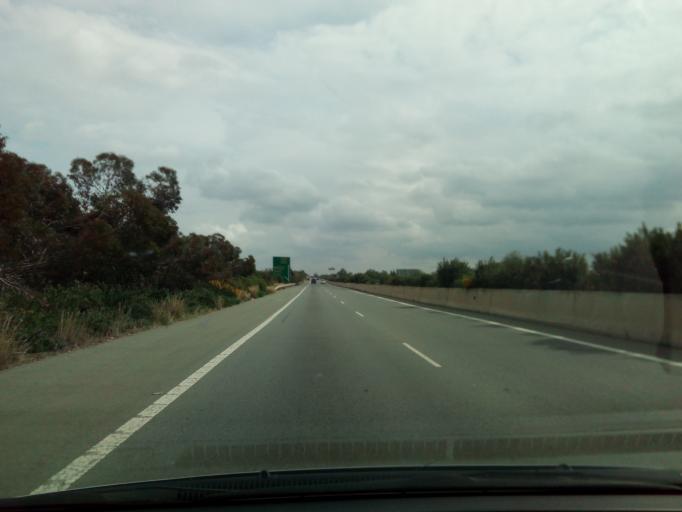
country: CY
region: Lefkosia
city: Kato Deftera
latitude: 35.1339
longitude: 33.2846
